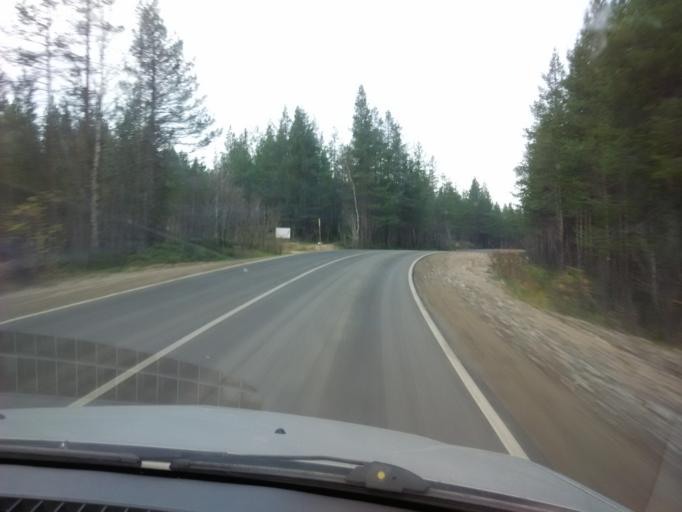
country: RU
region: Murmansk
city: Kandalaksha
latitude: 67.2365
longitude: 32.4088
